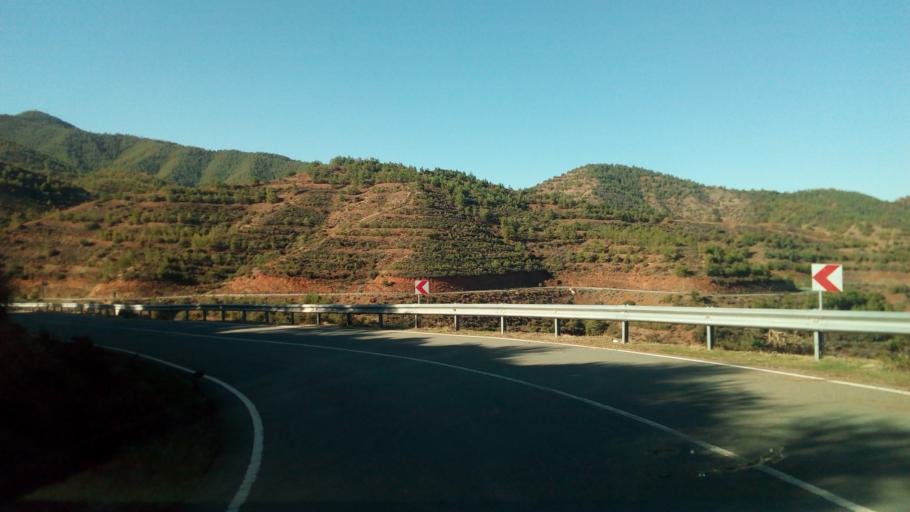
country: CY
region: Lefkosia
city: Lefka
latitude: 35.1049
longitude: 32.7567
